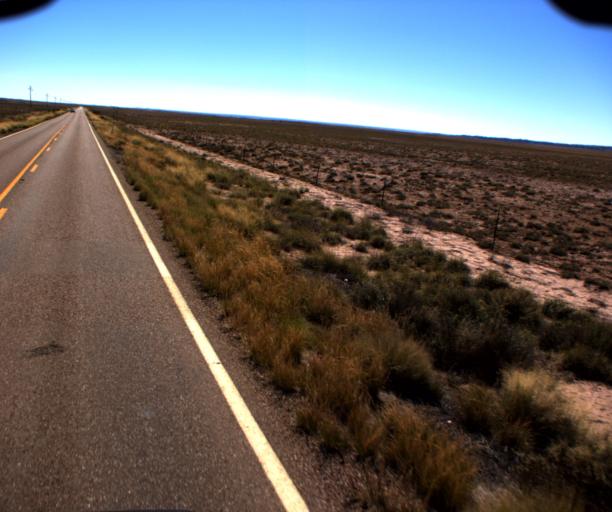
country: US
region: Arizona
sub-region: Navajo County
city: Holbrook
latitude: 35.1039
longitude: -110.0953
